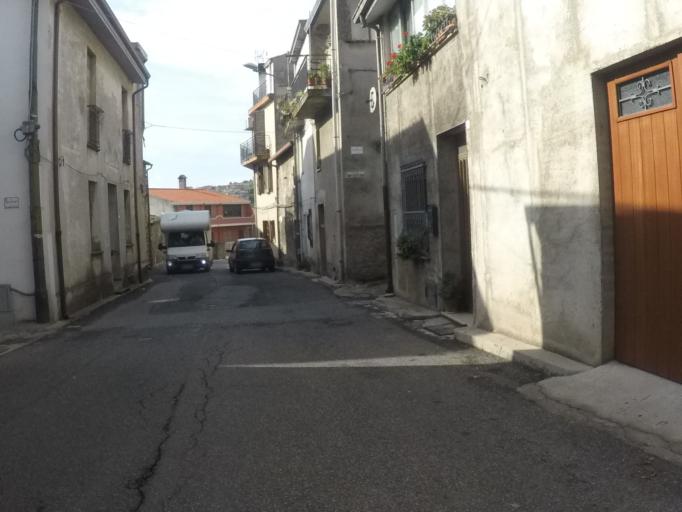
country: IT
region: Sardinia
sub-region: Provincia di Oristano
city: Santu Lussurgiu
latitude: 40.1412
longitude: 8.6512
